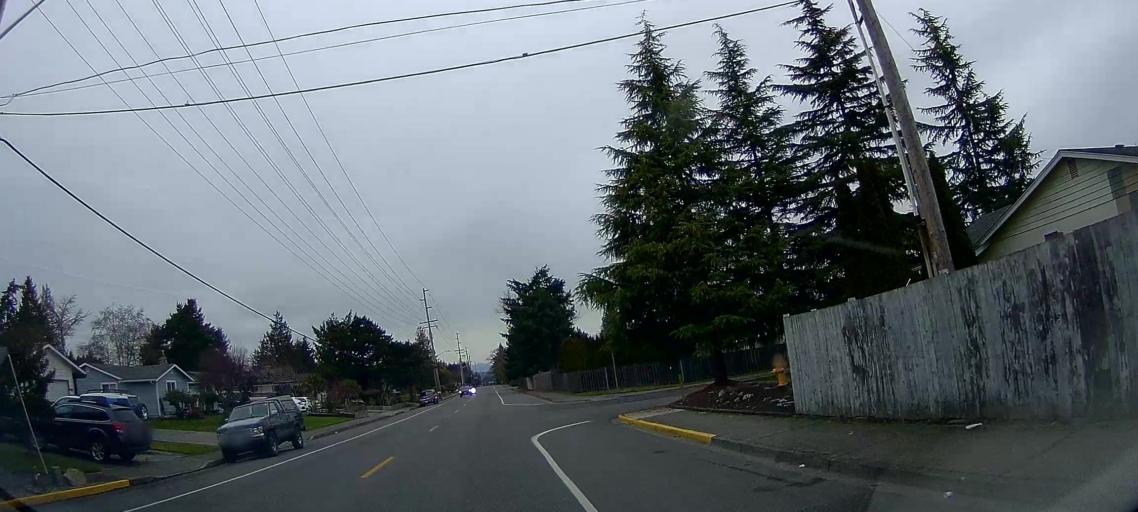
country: US
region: Washington
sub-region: Skagit County
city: Mount Vernon
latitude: 48.4227
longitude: -122.3188
